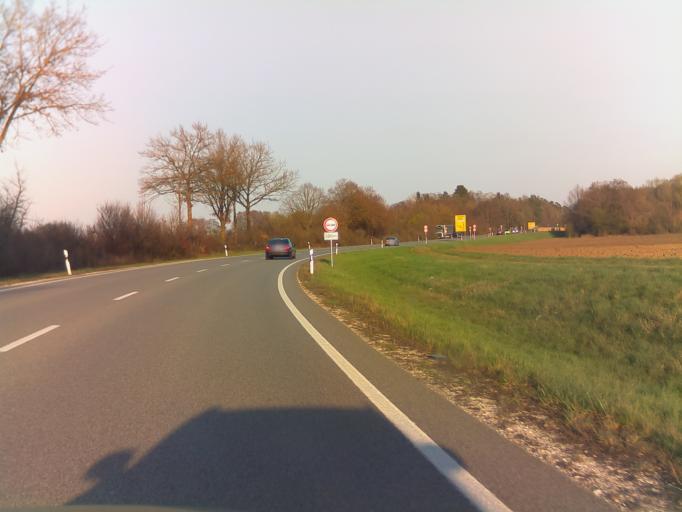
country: DE
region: Bavaria
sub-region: Upper Bavaria
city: Ernsgaden
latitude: 48.7289
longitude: 11.5560
